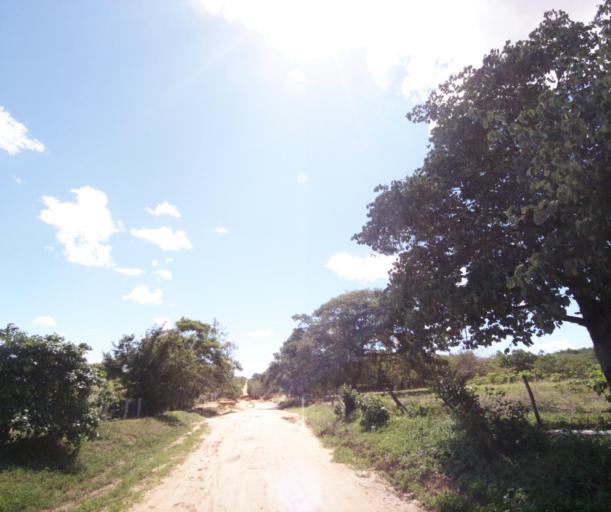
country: BR
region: Bahia
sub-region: Carinhanha
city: Carinhanha
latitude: -14.2361
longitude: -44.3188
